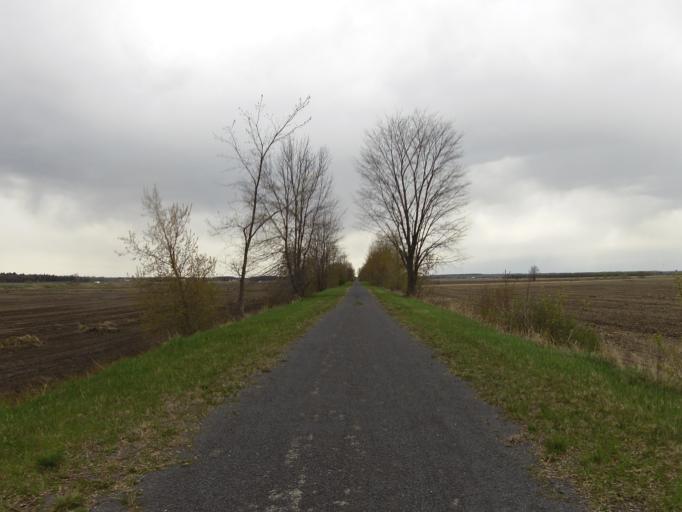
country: CA
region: Ontario
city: Bourget
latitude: 45.4518
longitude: -75.1026
